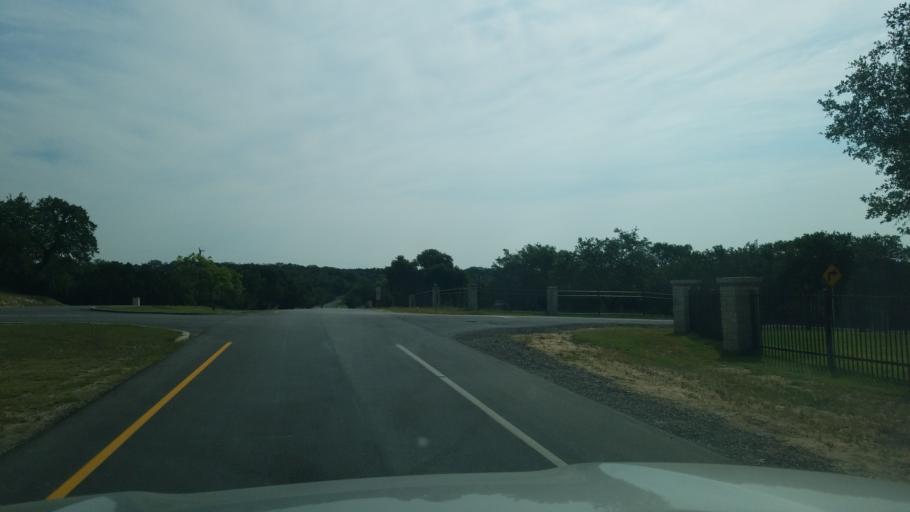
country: US
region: Texas
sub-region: Bexar County
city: Scenic Oaks
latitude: 29.7210
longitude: -98.6626
